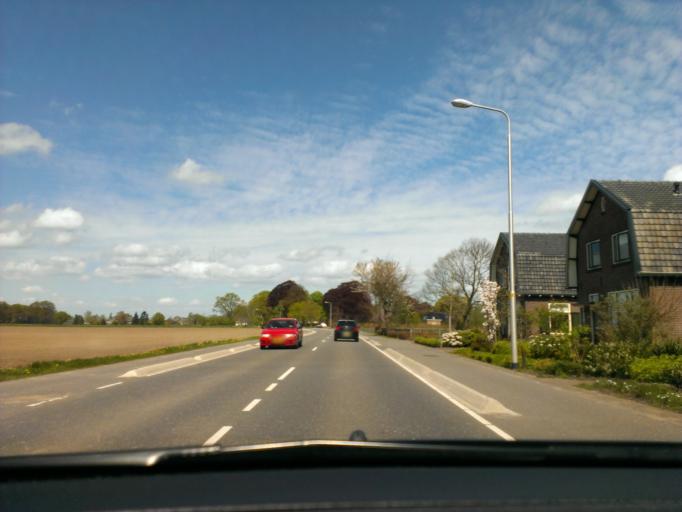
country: NL
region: Gelderland
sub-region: Gemeente Voorst
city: Twello
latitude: 52.2561
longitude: 6.1109
